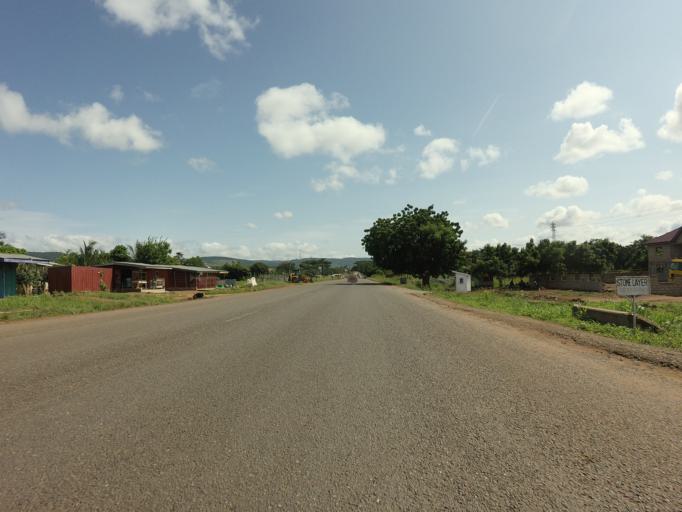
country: GH
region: Eastern
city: Aburi
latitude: 5.8470
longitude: -0.1143
